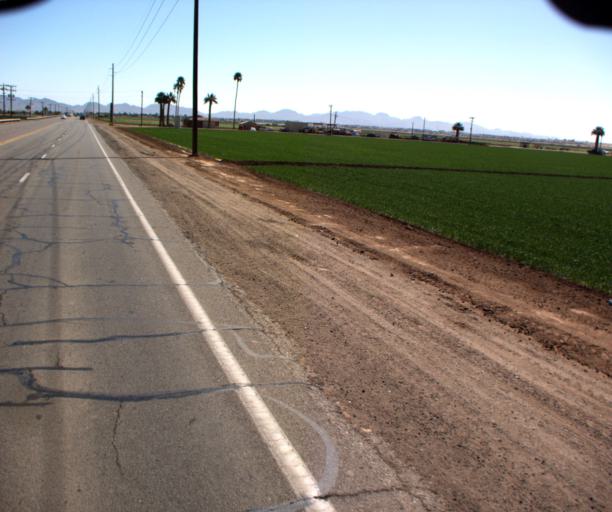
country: US
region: Arizona
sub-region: Yuma County
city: Yuma
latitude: 32.6988
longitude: -114.5665
